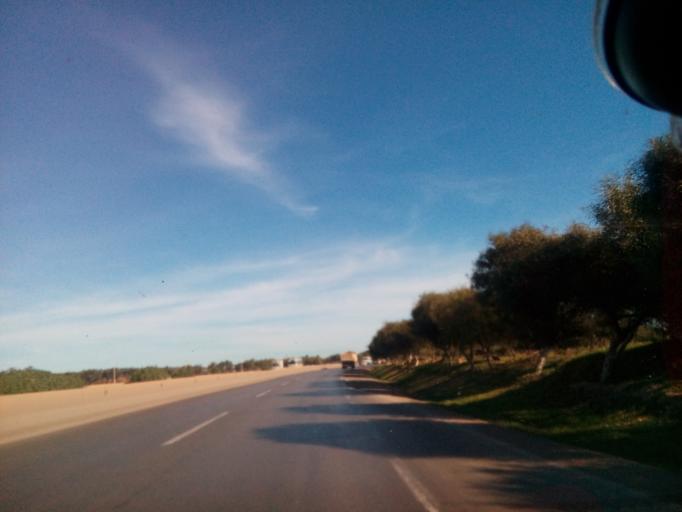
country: DZ
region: Oran
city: Ain el Bya
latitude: 35.7868
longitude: -0.4105
